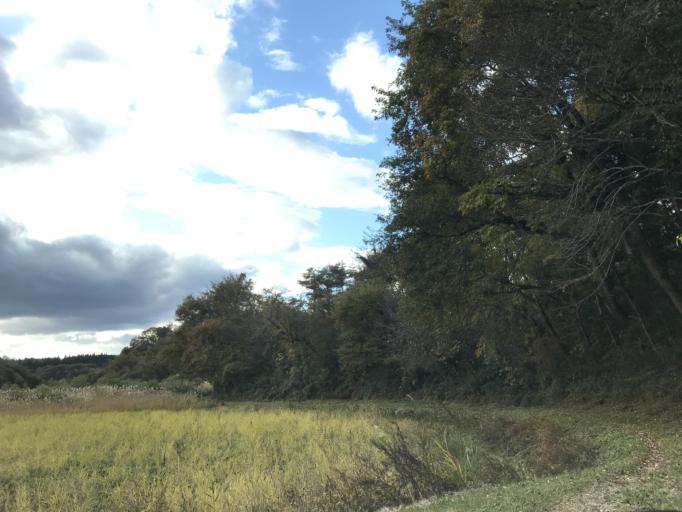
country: JP
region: Iwate
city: Ichinoseki
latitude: 38.8769
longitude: 141.1284
